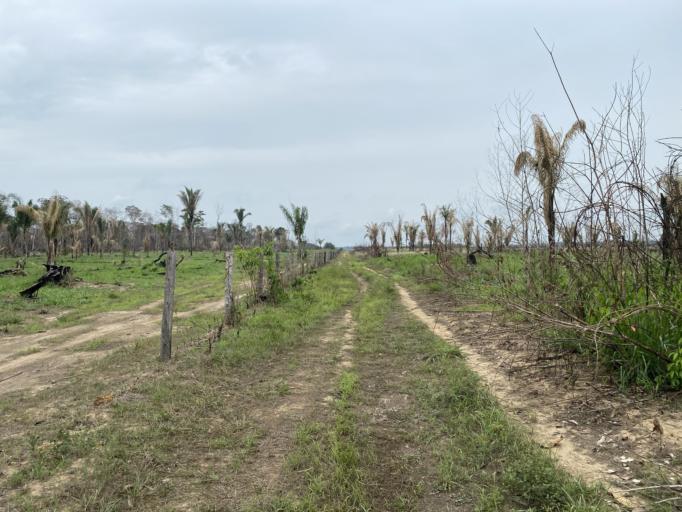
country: BR
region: Rondonia
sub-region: Porto Velho
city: Porto Velho
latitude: -8.7520
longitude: -64.0537
